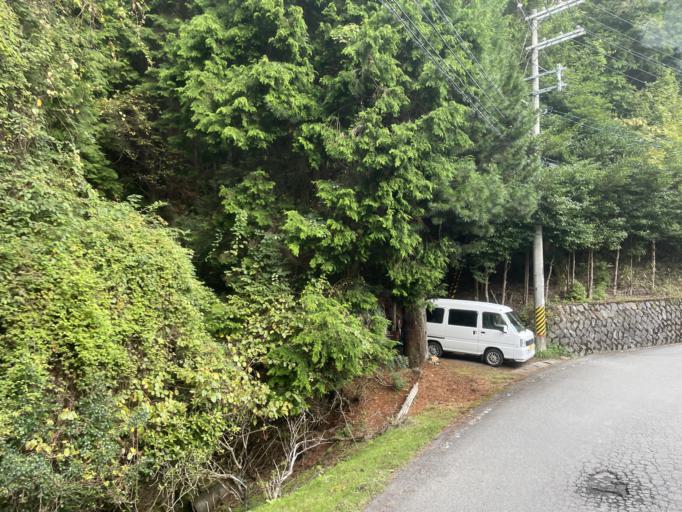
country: JP
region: Wakayama
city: Koya
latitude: 34.2267
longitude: 135.5761
